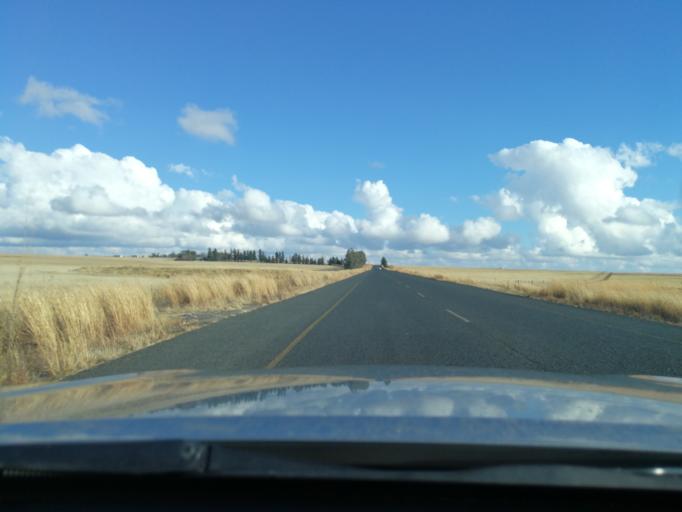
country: ZA
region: Orange Free State
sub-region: Thabo Mofutsanyana District Municipality
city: Bethlehem
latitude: -28.0585
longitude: 28.3638
